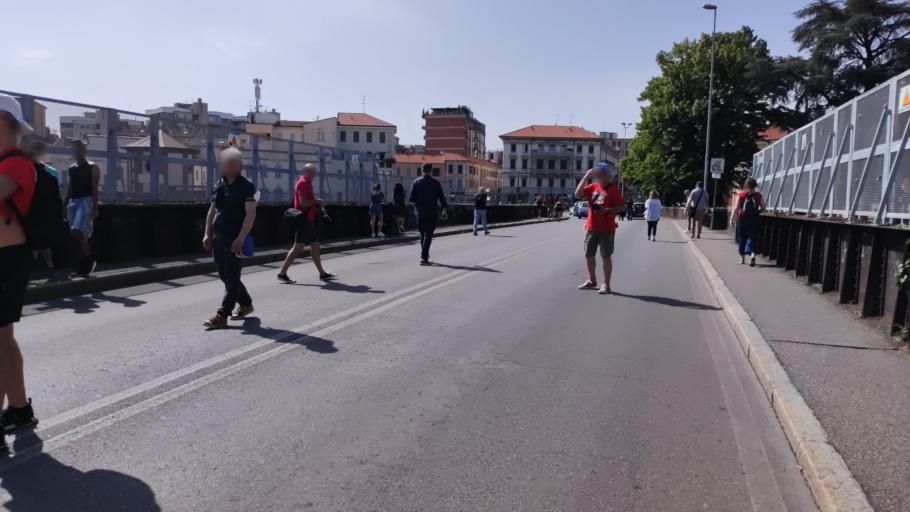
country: IT
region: Lombardy
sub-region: Provincia di Monza e Brianza
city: Monza
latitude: 45.5794
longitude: 9.2748
